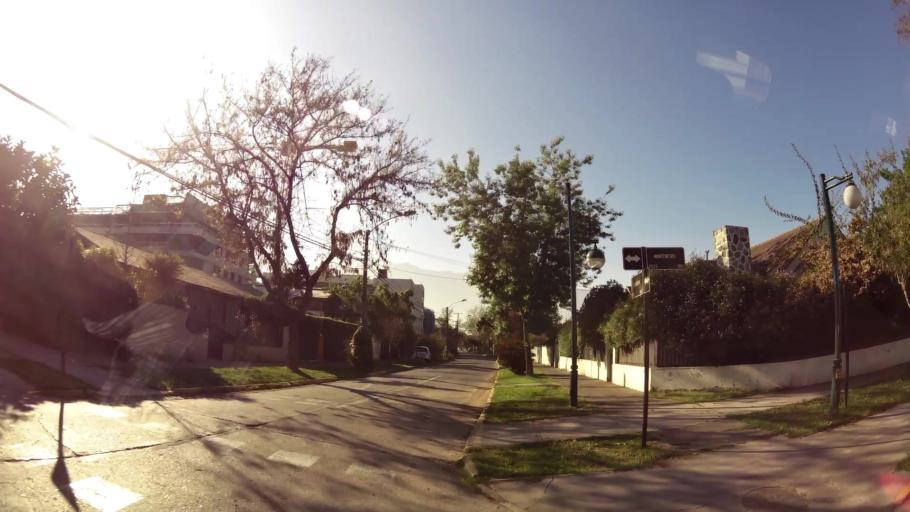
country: CL
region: Santiago Metropolitan
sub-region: Provincia de Santiago
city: Villa Presidente Frei, Nunoa, Santiago, Chile
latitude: -33.4379
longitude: -70.5824
